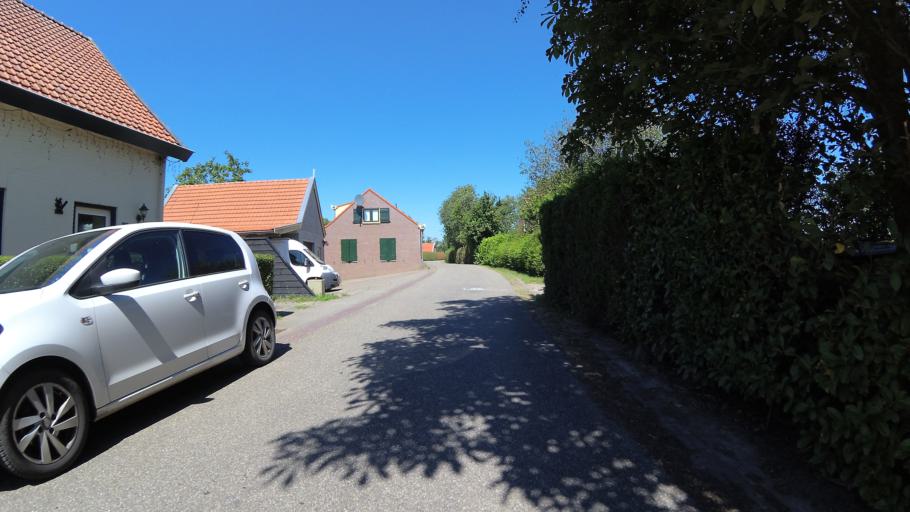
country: NL
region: North Brabant
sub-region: Gemeente Waalwijk
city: Waspik
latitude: 51.7177
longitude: 5.0054
